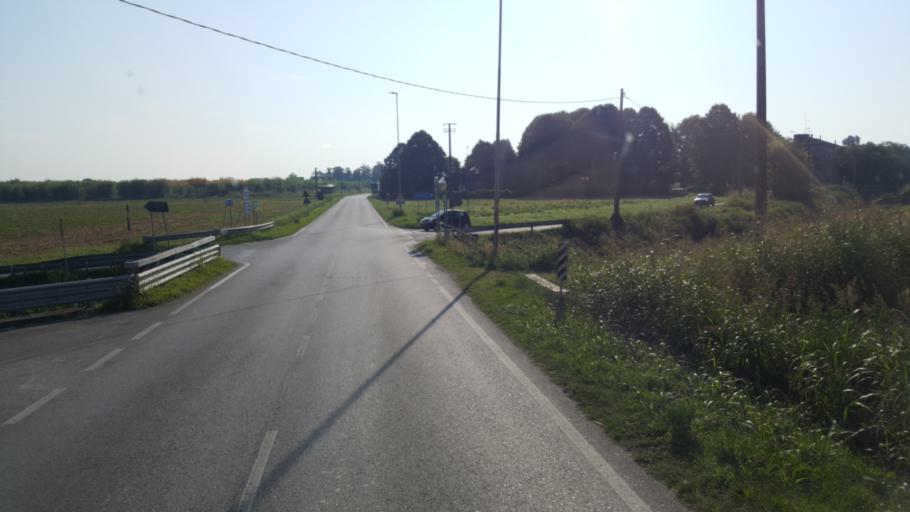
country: IT
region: Lombardy
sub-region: Provincia di Cremona
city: Casalbuttano
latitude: 45.2580
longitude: 9.9607
